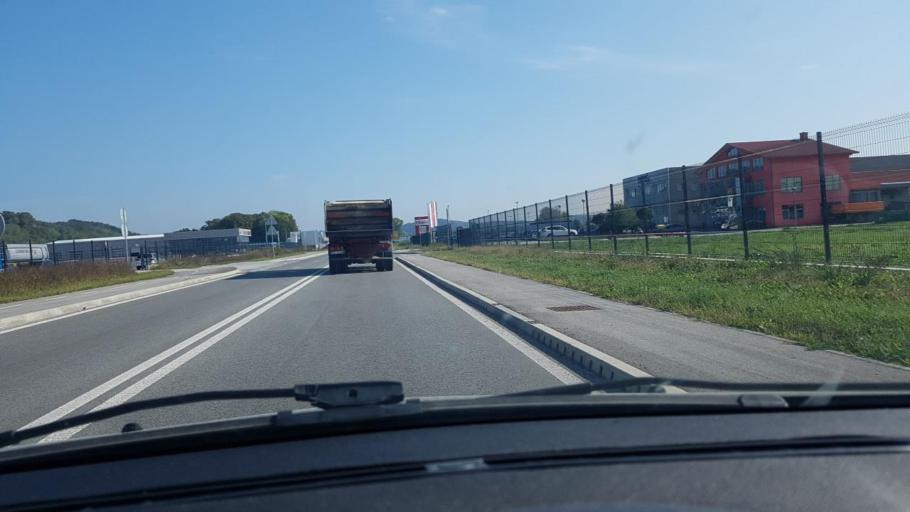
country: HR
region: Krapinsko-Zagorska
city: Oroslavje
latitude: 46.0116
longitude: 15.8816
